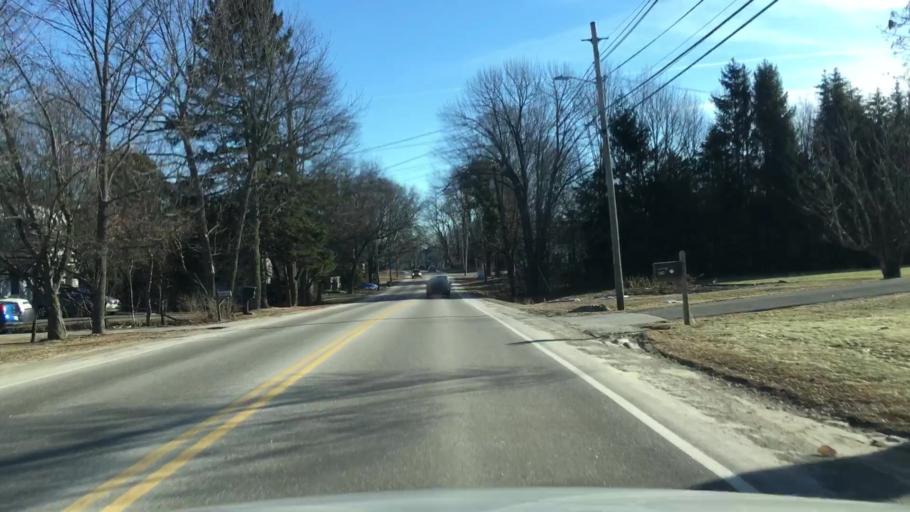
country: US
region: Maine
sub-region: Penobscot County
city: Bangor
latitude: 44.8152
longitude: -68.7979
